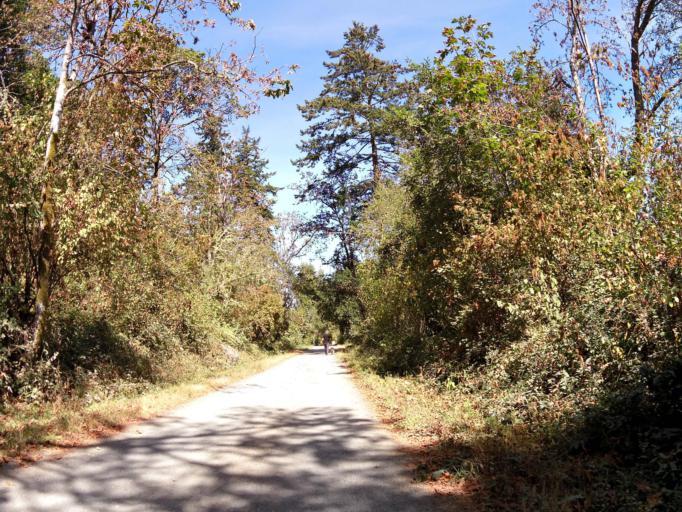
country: CA
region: British Columbia
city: Victoria
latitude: 48.4966
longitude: -123.3604
